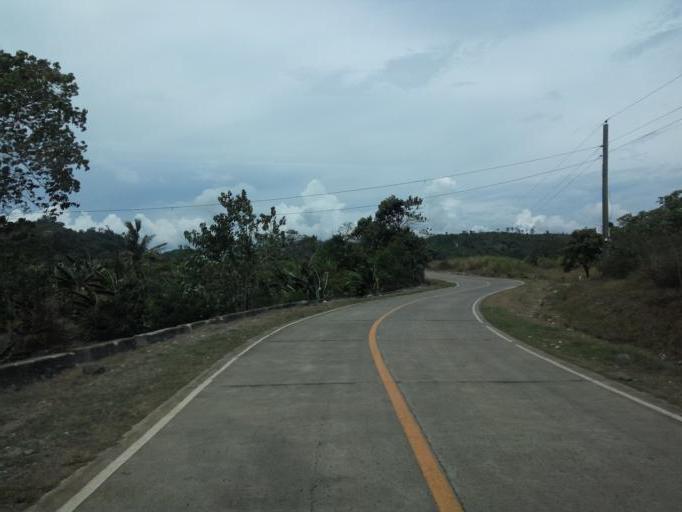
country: PH
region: Cagayan Valley
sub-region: Province of Quirino
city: Dumabato
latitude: 16.2575
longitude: 121.6686
